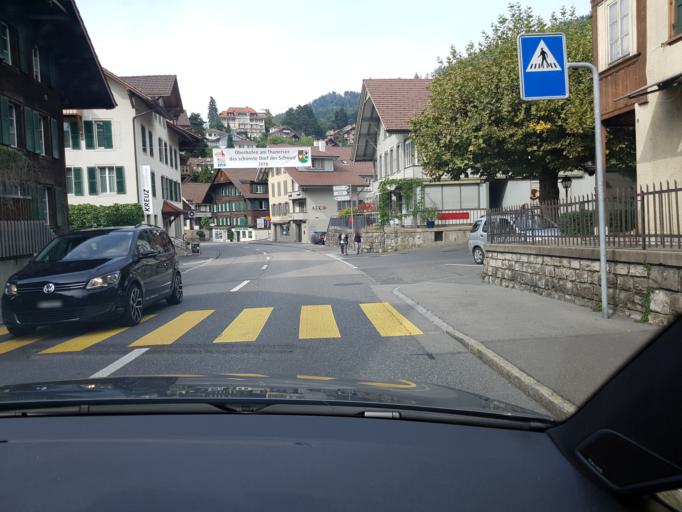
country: CH
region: Bern
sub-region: Thun District
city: Hilterfingen
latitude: 46.7303
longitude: 7.6693
